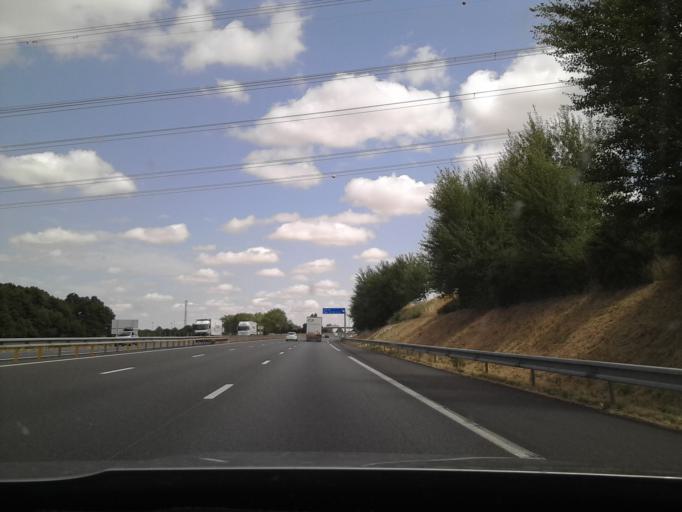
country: FR
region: Centre
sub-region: Departement d'Indre-et-Loire
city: Parcay-Meslay
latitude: 47.4703
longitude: 0.7699
